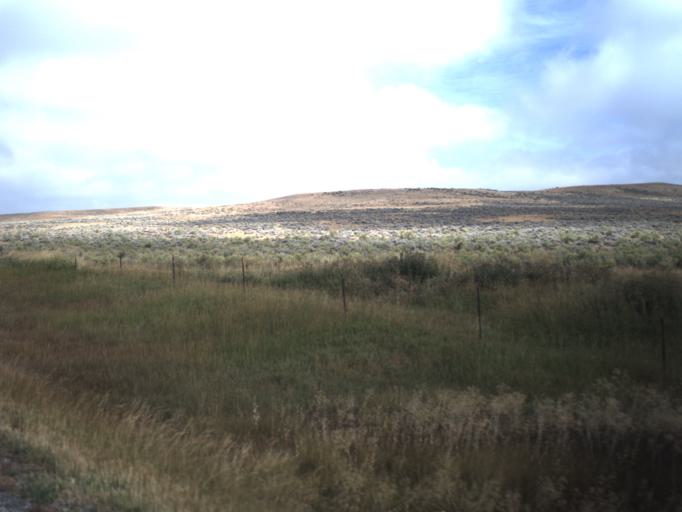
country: US
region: Utah
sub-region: Rich County
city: Randolph
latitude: 41.4720
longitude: -111.1084
